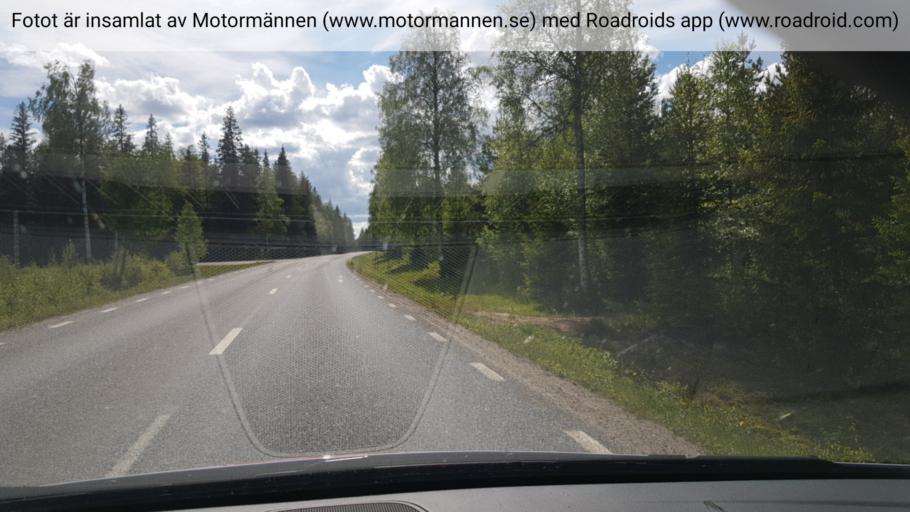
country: SE
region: Vaesterbotten
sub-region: Skelleftea Kommun
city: Burtraesk
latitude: 64.4091
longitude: 20.3930
